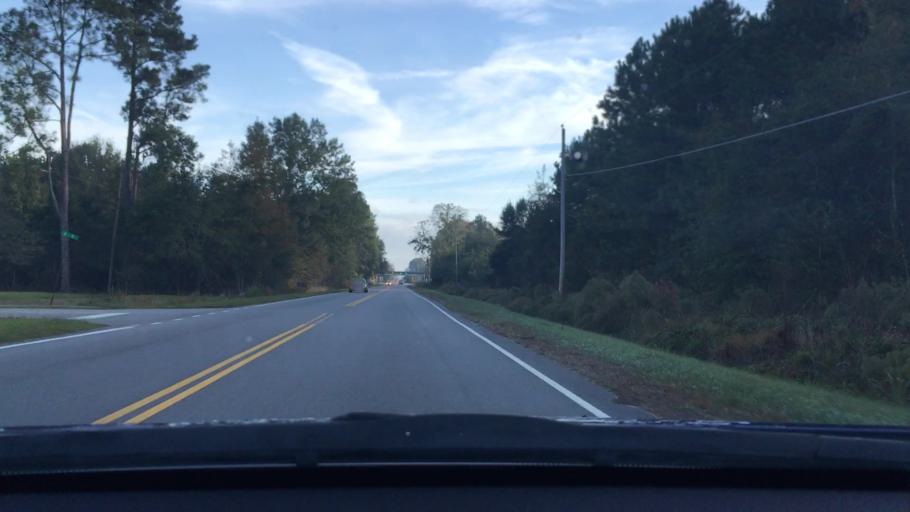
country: US
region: South Carolina
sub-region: Sumter County
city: Sumter
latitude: 33.9332
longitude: -80.3223
